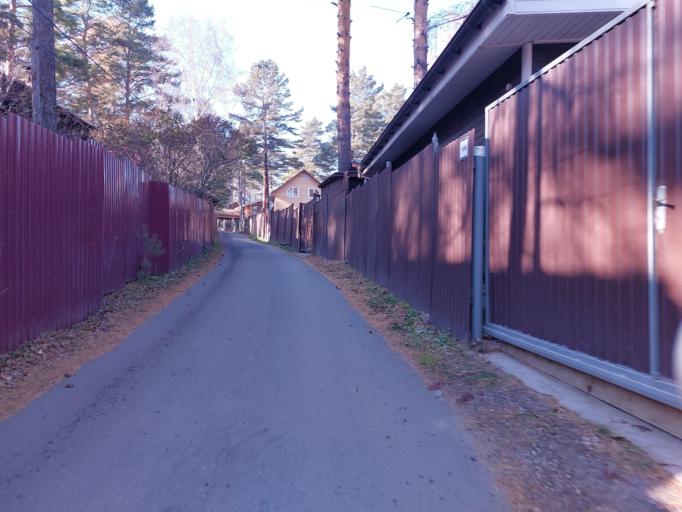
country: RU
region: Irkutsk
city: Pivovarikha
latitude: 52.1895
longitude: 104.4667
